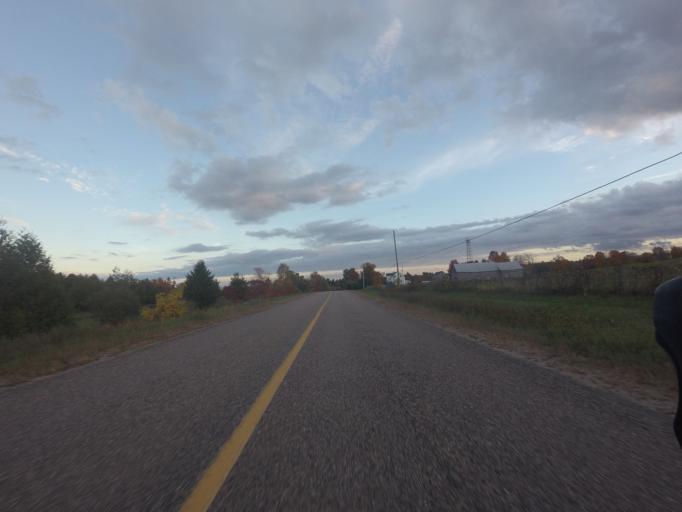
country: CA
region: Ontario
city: Renfrew
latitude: 45.4109
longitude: -76.9532
